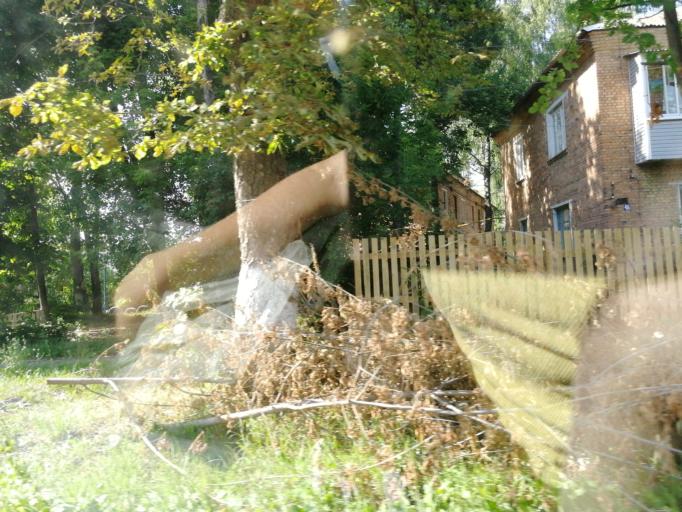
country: RU
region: Tula
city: Bogoroditsk
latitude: 53.7661
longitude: 38.1234
